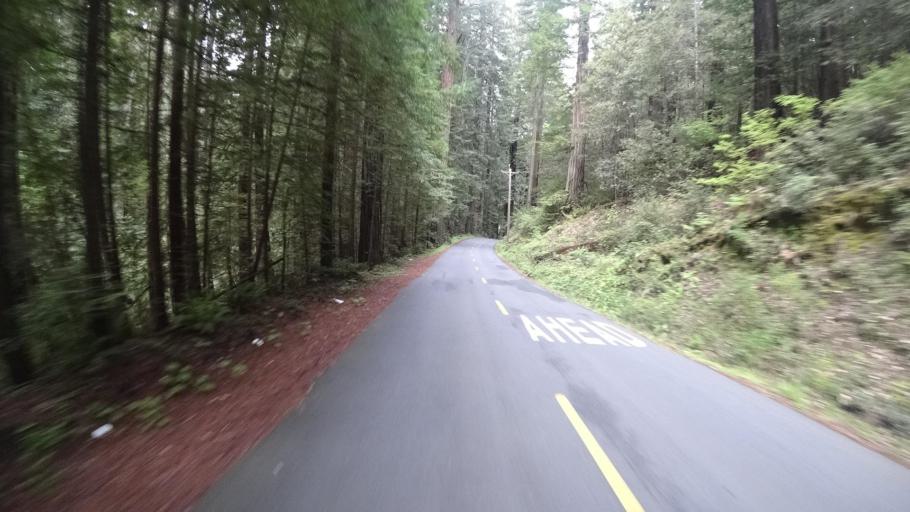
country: US
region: California
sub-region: Humboldt County
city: Redway
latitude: 40.2795
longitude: -123.8516
